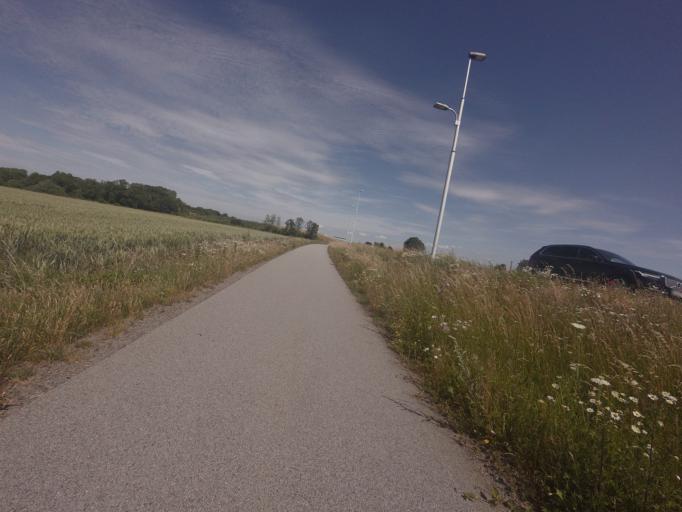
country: SE
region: Skane
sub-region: Malmo
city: Bunkeflostrand
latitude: 55.5418
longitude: 12.9803
